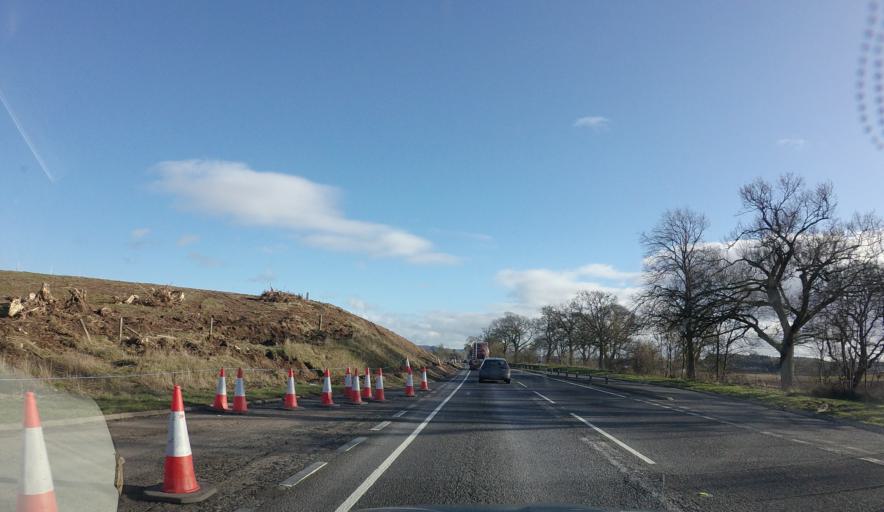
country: GB
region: Scotland
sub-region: Perth and Kinross
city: Bankfoot
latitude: 56.4855
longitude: -3.4997
